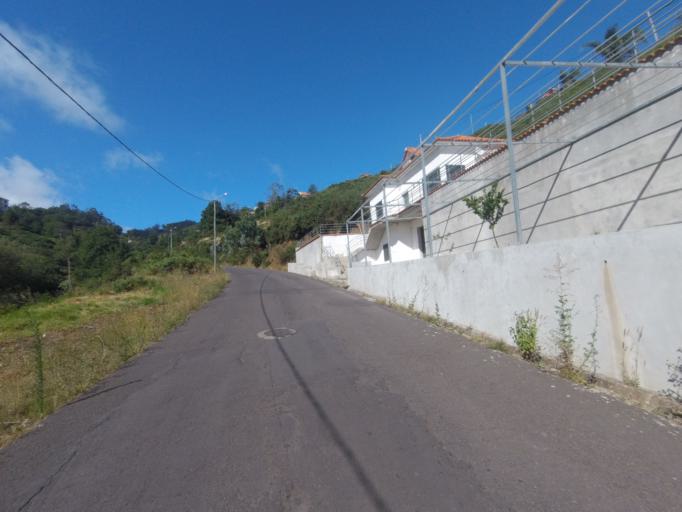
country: PT
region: Madeira
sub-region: Ribeira Brava
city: Campanario
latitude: 32.6931
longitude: -17.0188
